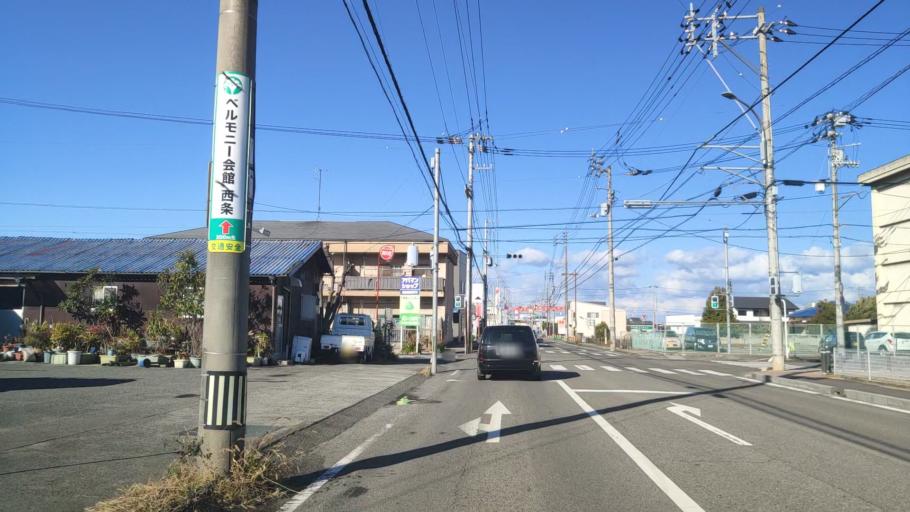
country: JP
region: Ehime
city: Saijo
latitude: 33.9181
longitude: 133.1919
